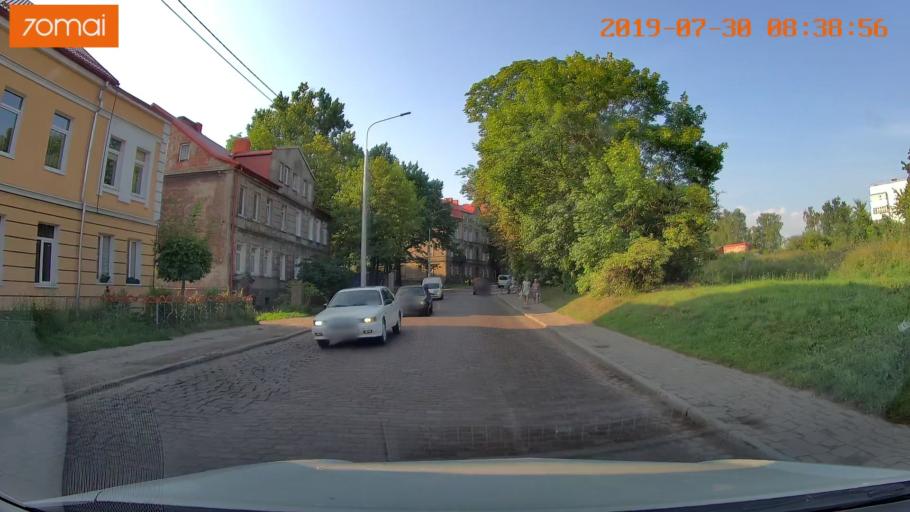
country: RU
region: Kaliningrad
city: Chernyakhovsk
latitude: 54.6326
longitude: 21.8030
